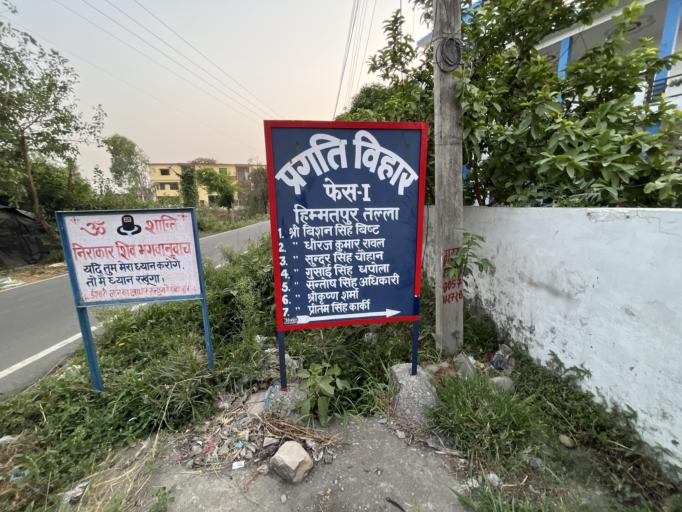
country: IN
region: Uttarakhand
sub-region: Naini Tal
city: Haldwani
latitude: 29.2178
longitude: 79.4817
